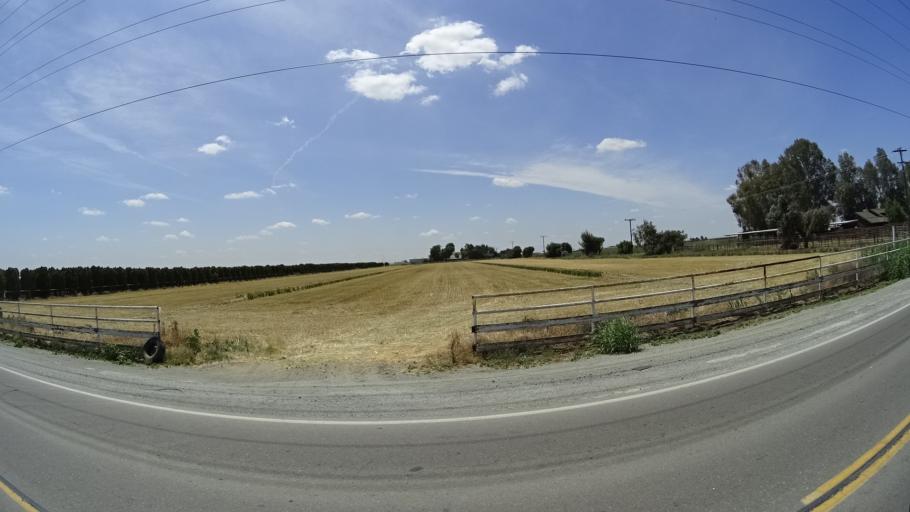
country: US
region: California
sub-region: Kings County
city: Home Garden
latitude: 36.2985
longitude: -119.6095
